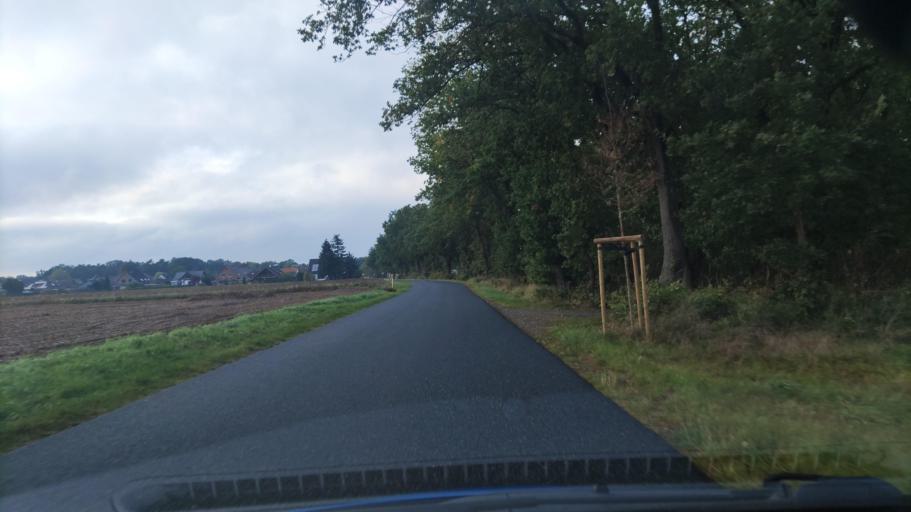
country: DE
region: Lower Saxony
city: Wrestedt
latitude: 52.9051
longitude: 10.6066
